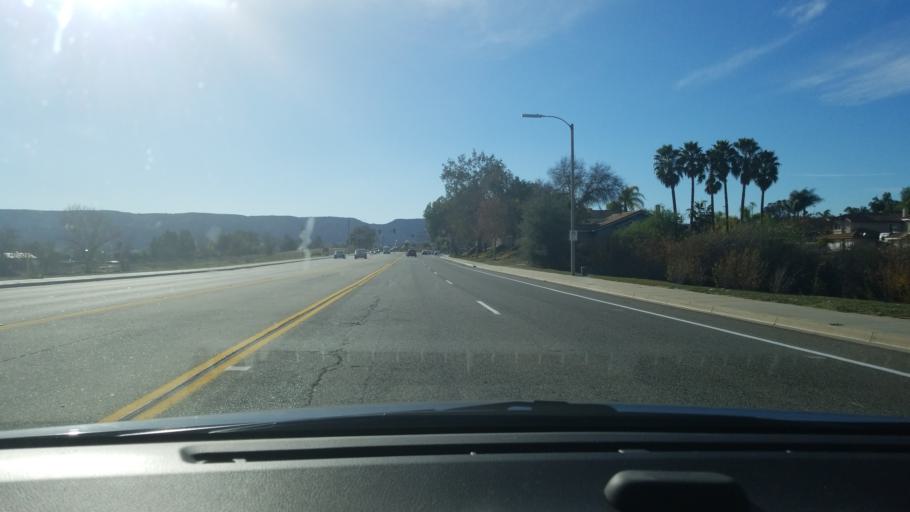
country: US
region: California
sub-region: Riverside County
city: Murrieta
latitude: 33.5636
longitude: -117.1930
